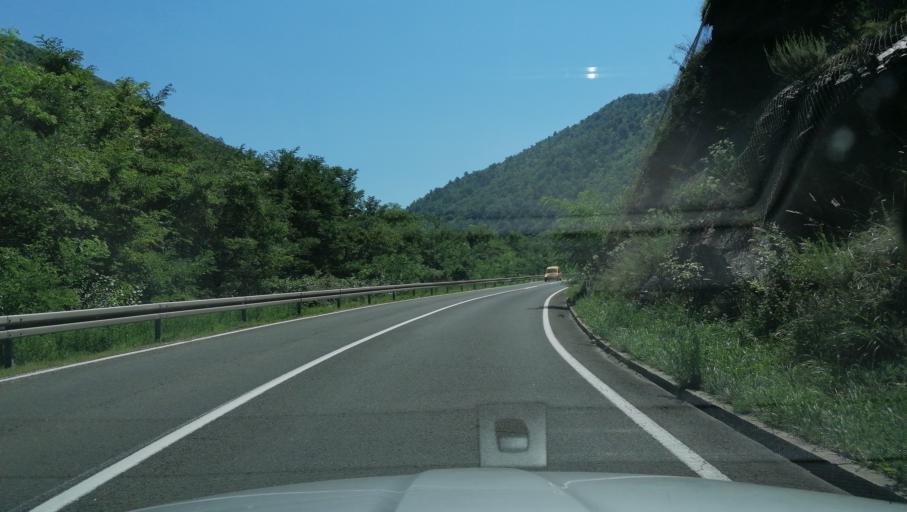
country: RS
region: Central Serbia
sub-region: Raski Okrug
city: Kraljevo
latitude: 43.5945
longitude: 20.5702
